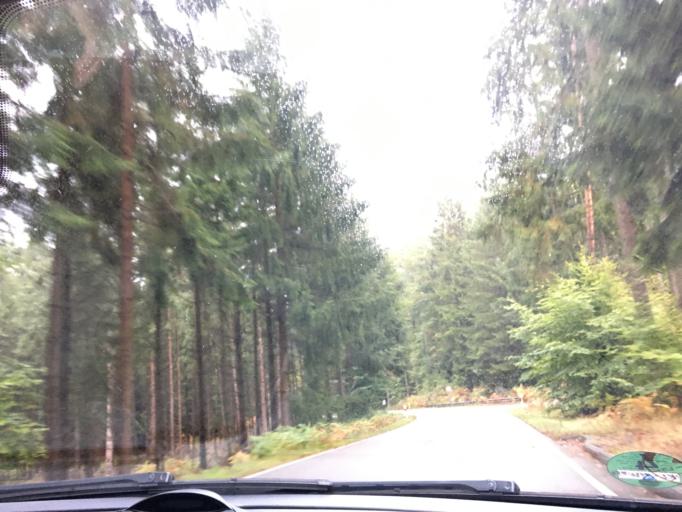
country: DE
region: Rheinland-Pfalz
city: Geiselberg
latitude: 49.3458
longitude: 7.7044
